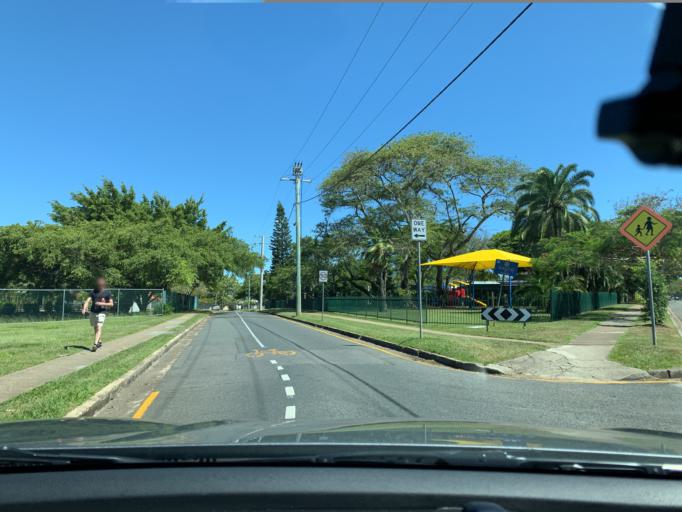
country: AU
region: Queensland
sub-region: Brisbane
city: Ascot
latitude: -27.4286
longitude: 153.0624
